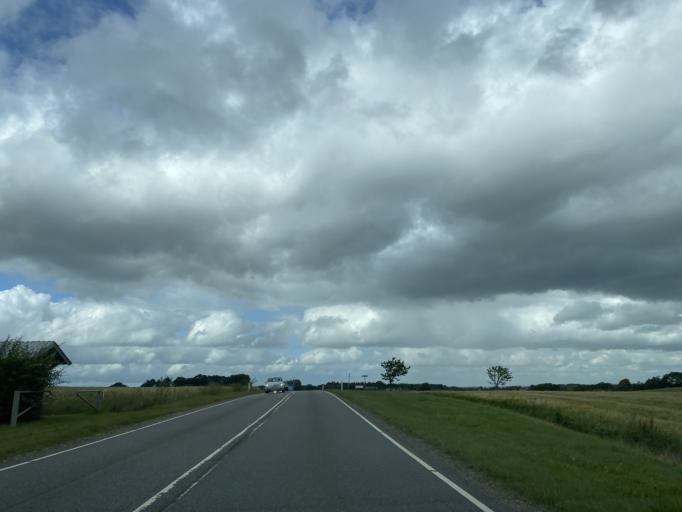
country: DK
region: Central Jutland
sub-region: Silkeborg Kommune
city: Silkeborg
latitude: 56.2385
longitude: 9.6232
